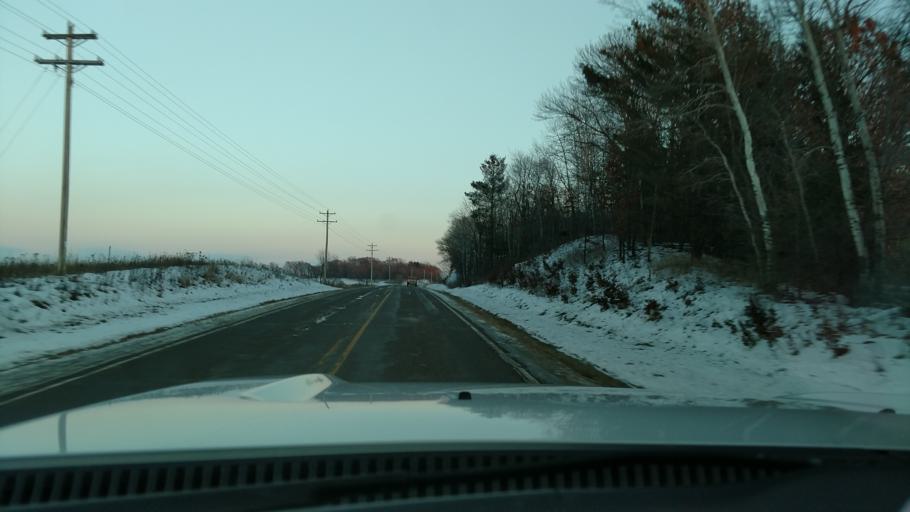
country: US
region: Wisconsin
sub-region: Saint Croix County
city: Roberts
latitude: 44.9135
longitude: -92.5310
